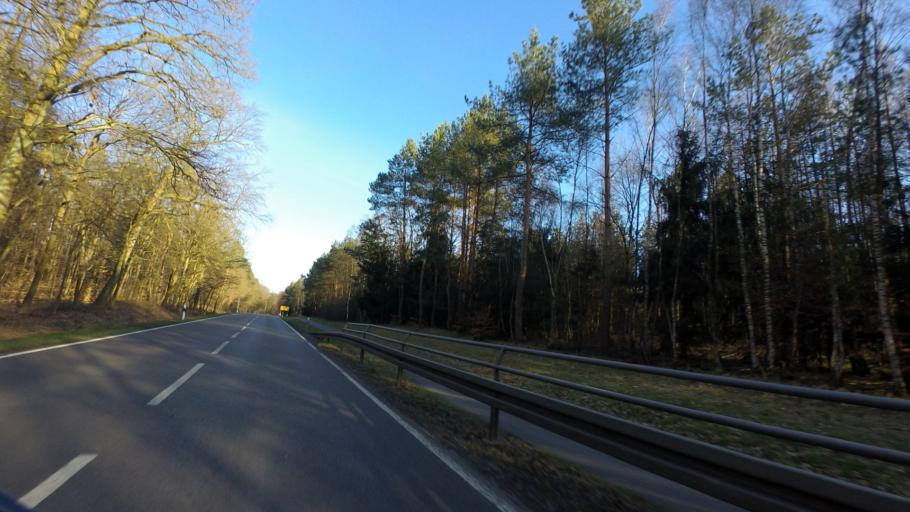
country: DE
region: Brandenburg
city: Britz
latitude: 52.8632
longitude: 13.8284
